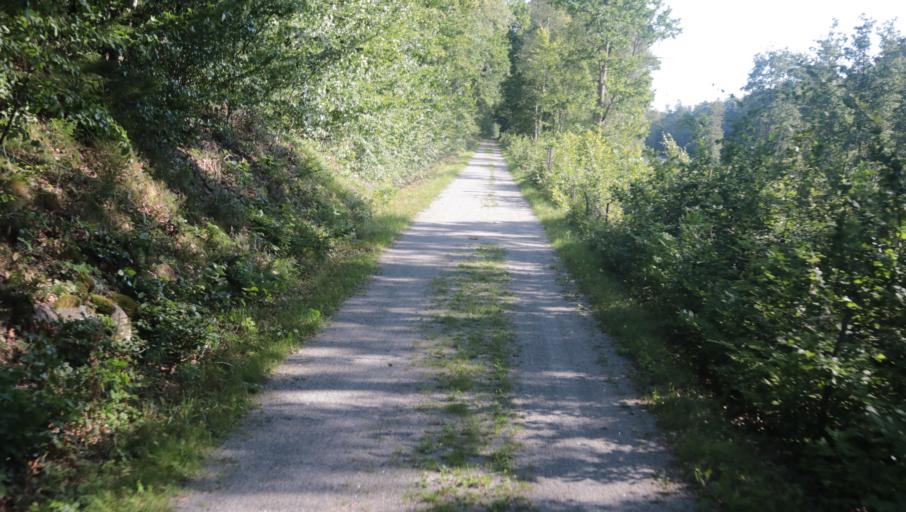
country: SE
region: Blekinge
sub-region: Karlshamns Kommun
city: Svangsta
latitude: 56.3680
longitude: 14.6850
